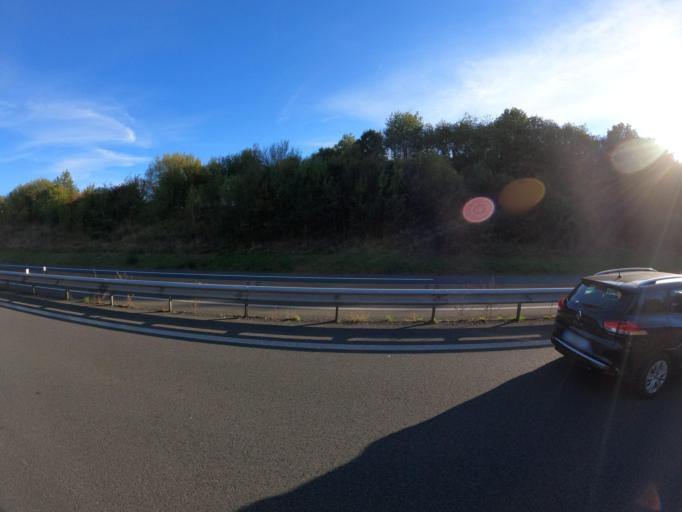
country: FR
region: Pays de la Loire
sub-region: Departement de Maine-et-Loire
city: Saint-Lambert-du-Lattay
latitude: 47.2412
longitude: -0.6478
